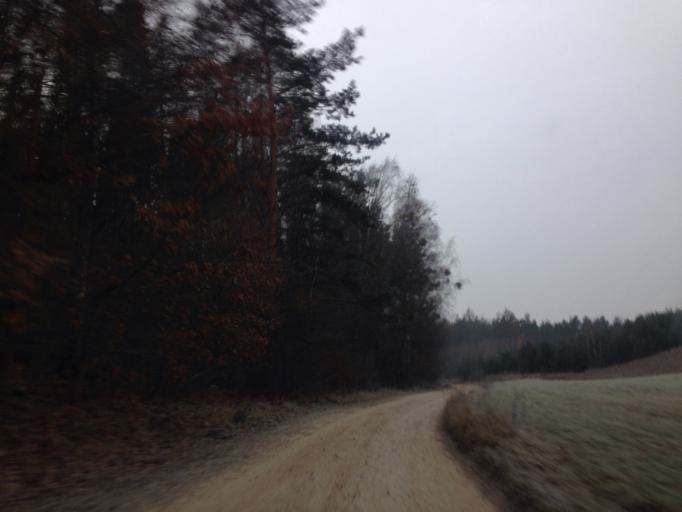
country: PL
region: Kujawsko-Pomorskie
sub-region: Powiat brodnicki
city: Gorzno
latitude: 53.2222
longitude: 19.6458
